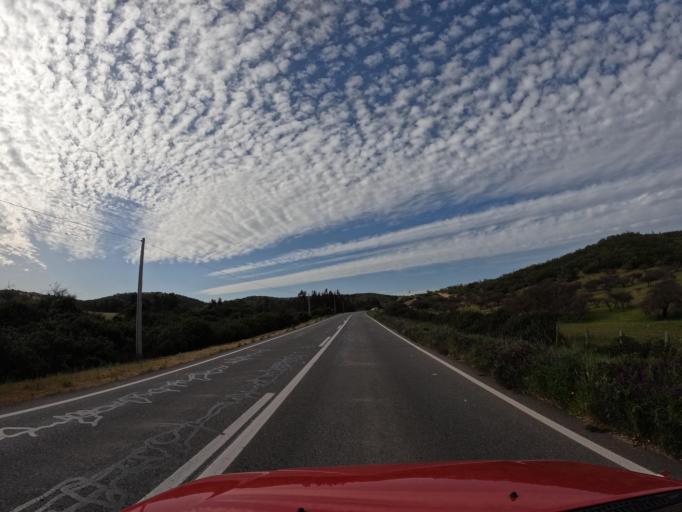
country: CL
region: O'Higgins
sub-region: Provincia de Colchagua
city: Santa Cruz
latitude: -34.3176
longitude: -71.7433
